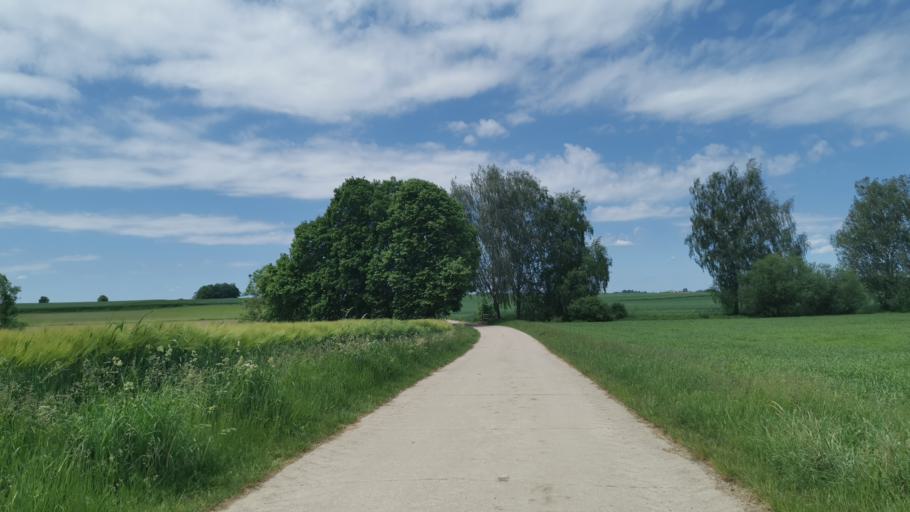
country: DE
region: Bavaria
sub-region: Swabia
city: Steindorf
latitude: 48.2390
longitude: 11.0143
